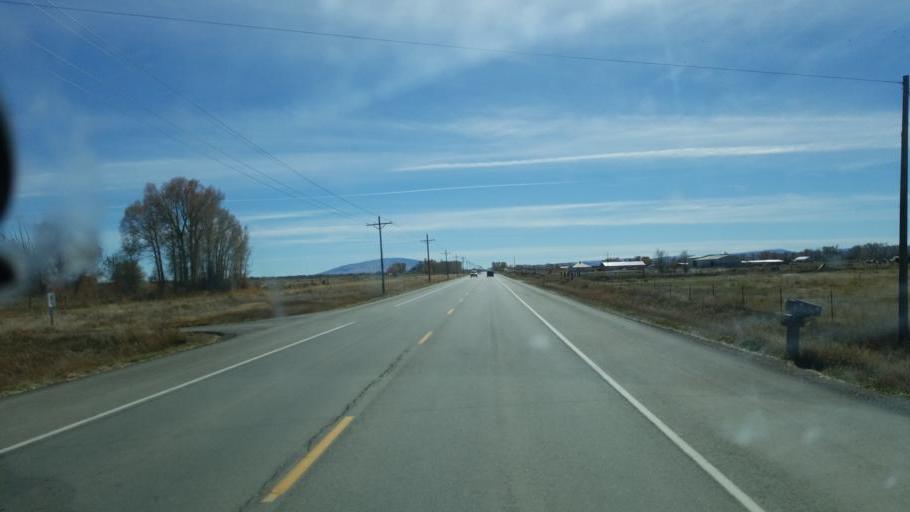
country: US
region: Colorado
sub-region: Conejos County
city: Conejos
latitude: 37.1459
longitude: -105.9953
